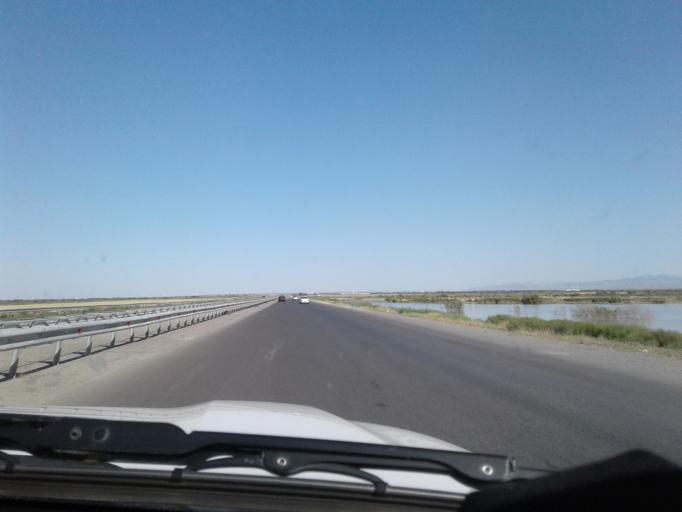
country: TM
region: Ahal
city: Kaka
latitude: 37.3943
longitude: 59.5707
